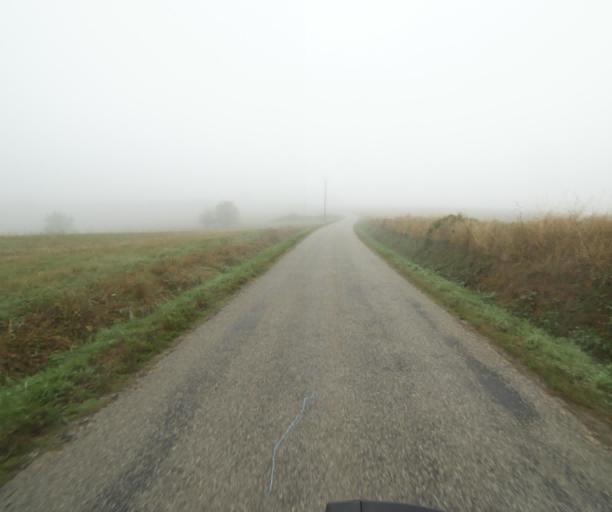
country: FR
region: Midi-Pyrenees
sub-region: Departement de la Haute-Garonne
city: Villemur-sur-Tarn
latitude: 43.9041
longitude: 1.4851
